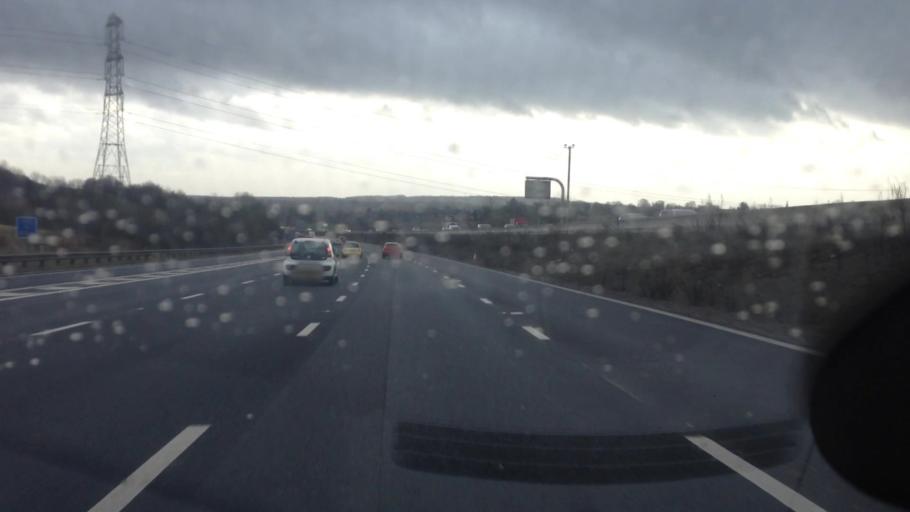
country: GB
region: England
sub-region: City and Borough of Wakefield
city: Horbury
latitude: 53.6766
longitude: -1.5527
